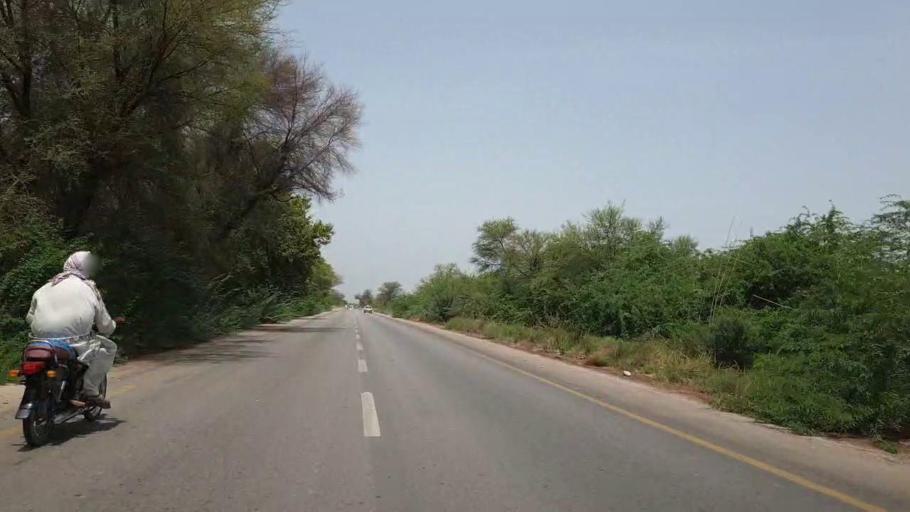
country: PK
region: Sindh
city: Nawabshah
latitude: 26.2116
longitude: 68.5178
